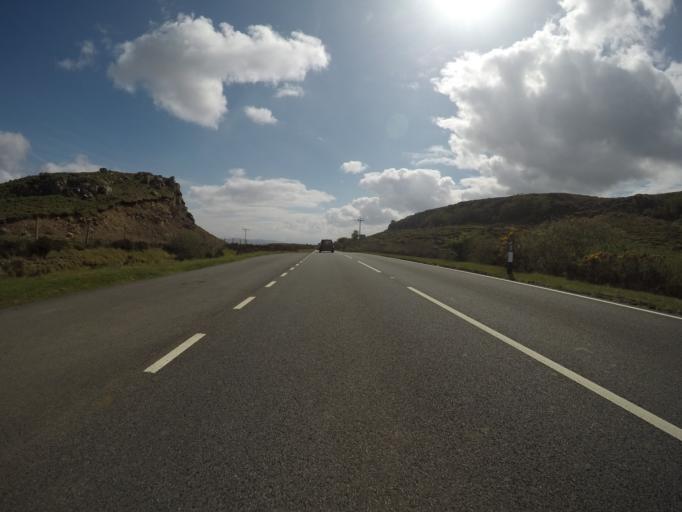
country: GB
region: Scotland
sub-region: Highland
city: Portree
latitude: 57.5161
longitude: -6.3419
